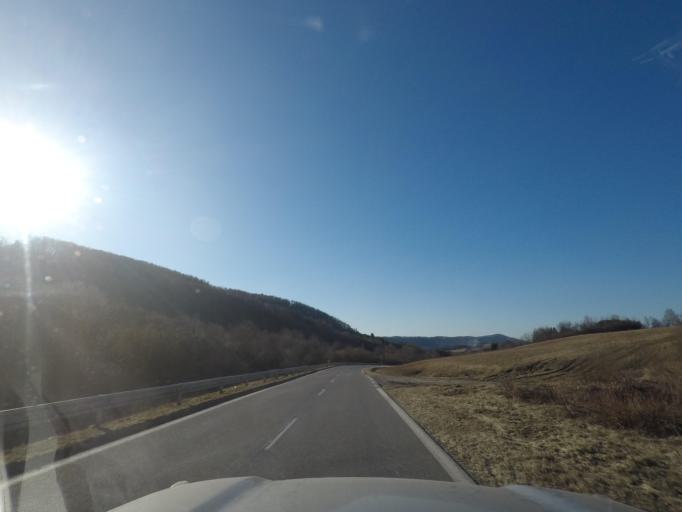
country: SK
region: Presovsky
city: Medzilaborce
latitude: 49.2416
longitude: 21.9389
